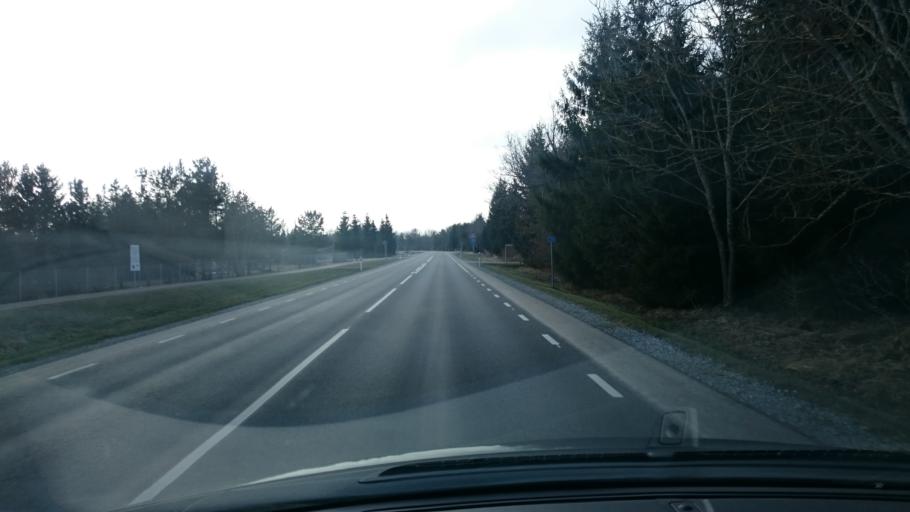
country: EE
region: Harju
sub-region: Paldiski linn
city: Paldiski
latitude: 59.3874
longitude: 24.2388
